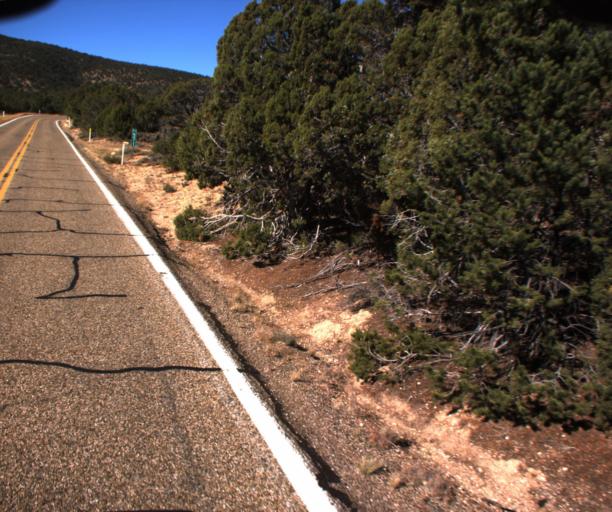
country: US
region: Arizona
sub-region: Coconino County
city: Fredonia
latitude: 36.7398
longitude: -112.1036
